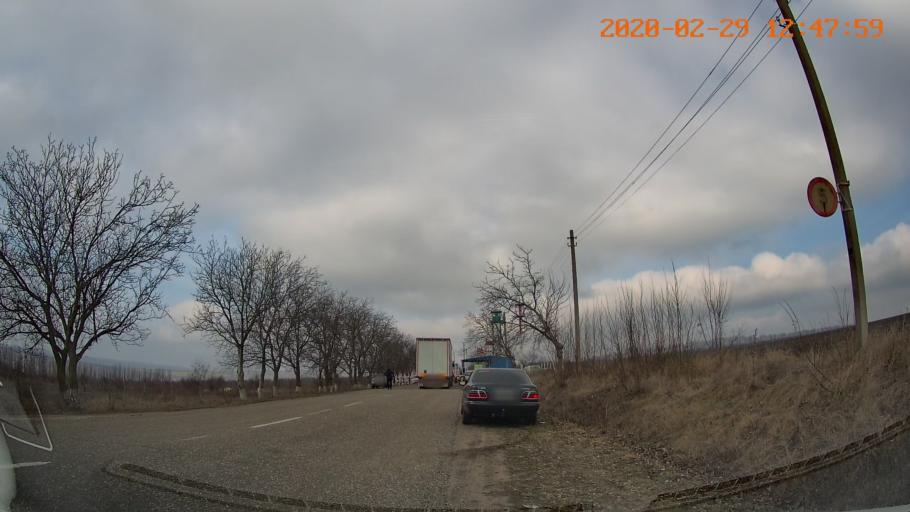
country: MD
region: Telenesti
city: Camenca
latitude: 48.1281
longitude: 28.7412
